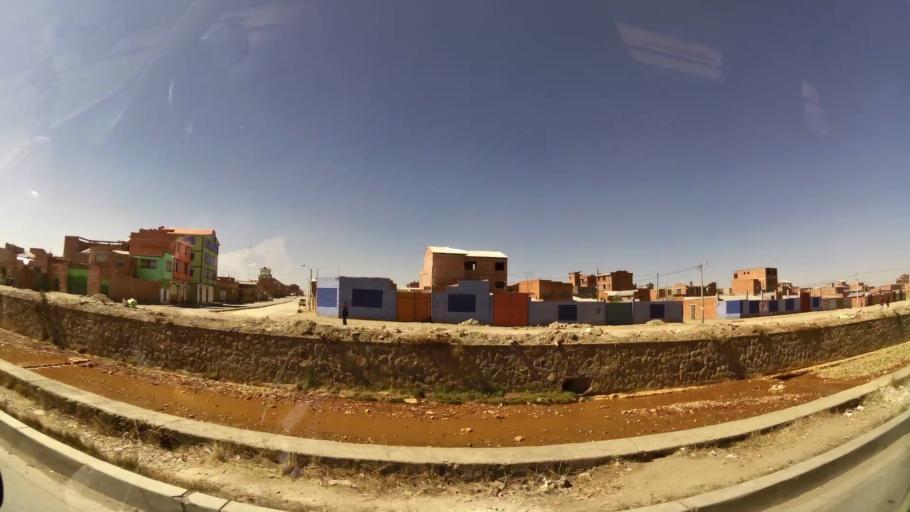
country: BO
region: La Paz
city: La Paz
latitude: -16.5005
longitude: -68.2089
